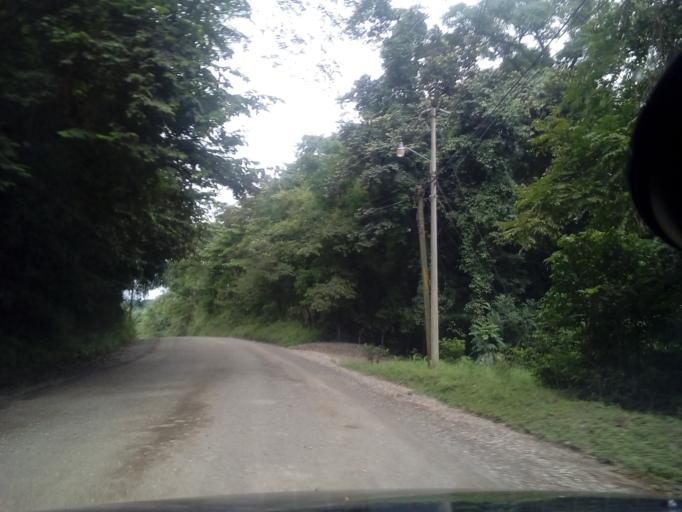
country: CR
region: Guanacaste
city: Samara
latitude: 9.9140
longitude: -85.5541
